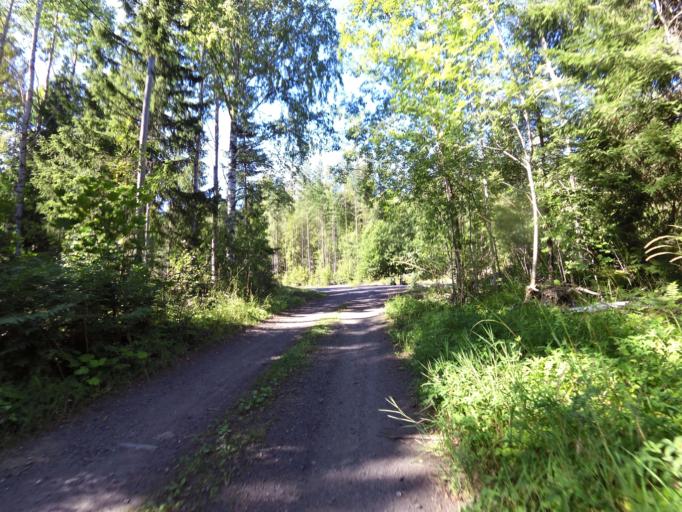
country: SE
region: Gaevleborg
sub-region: Hofors Kommun
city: Hofors
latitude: 60.5290
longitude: 16.4070
